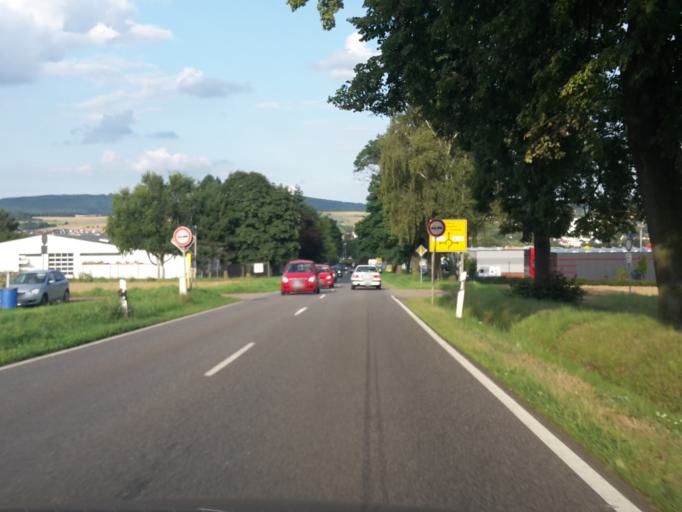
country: DE
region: Hesse
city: Bad Camberg
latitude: 50.2943
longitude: 8.2473
